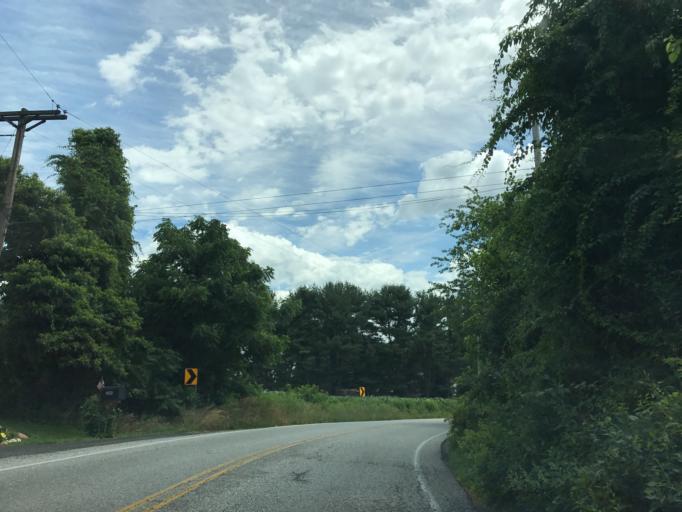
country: US
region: Maryland
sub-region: Harford County
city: Jarrettsville
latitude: 39.6019
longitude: -76.4946
